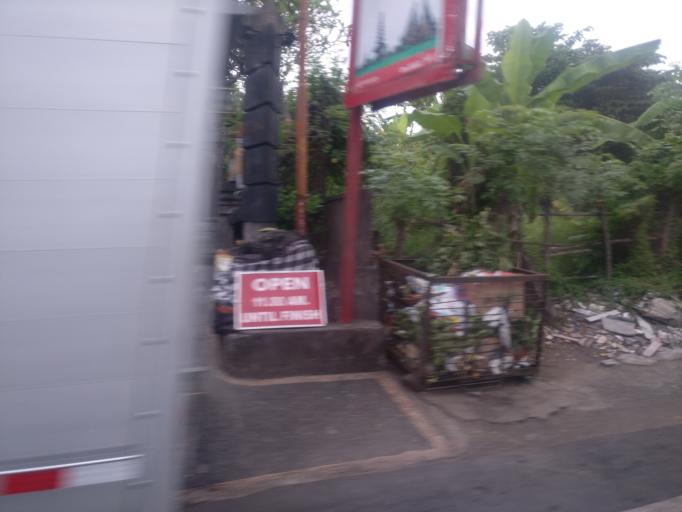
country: ID
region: Bali
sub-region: Kabupaten Gianyar
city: Ubud
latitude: -8.5303
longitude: 115.2718
